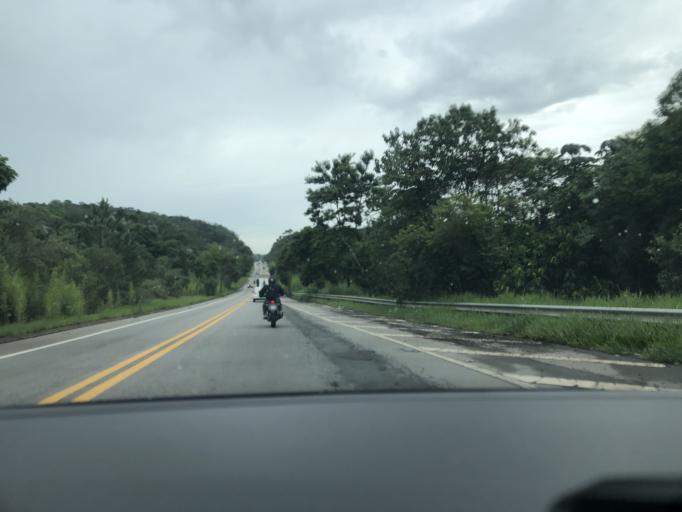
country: BR
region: Sao Paulo
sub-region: Jarinu
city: Jarinu
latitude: -23.1520
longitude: -46.7455
